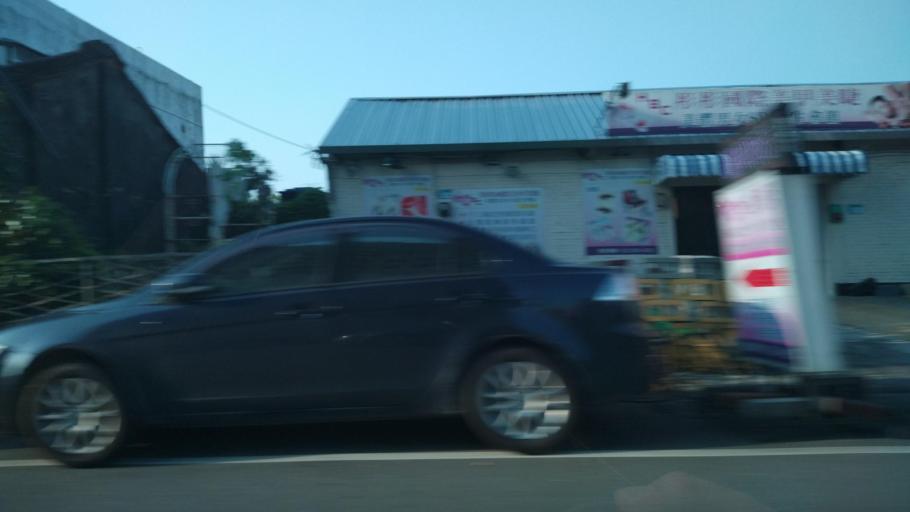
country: TW
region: Taipei
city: Taipei
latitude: 25.2596
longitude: 121.4992
